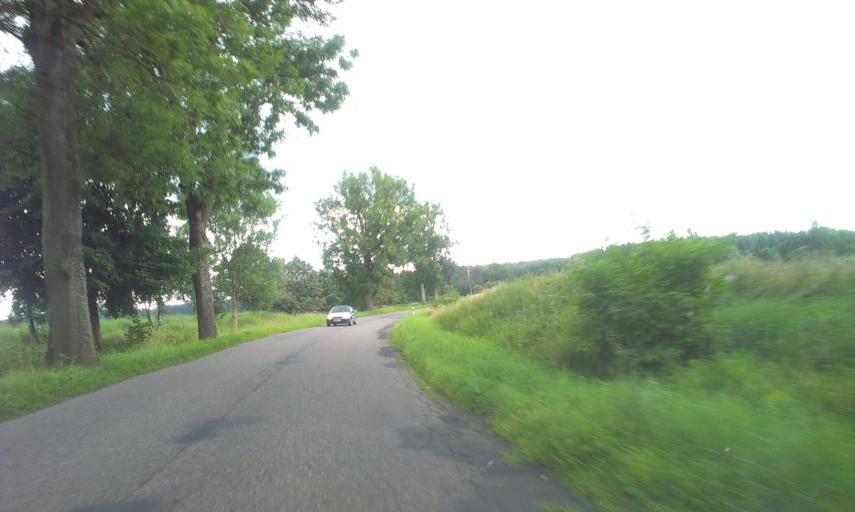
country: PL
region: West Pomeranian Voivodeship
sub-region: Powiat bialogardzki
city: Tychowo
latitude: 53.9083
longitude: 16.2424
